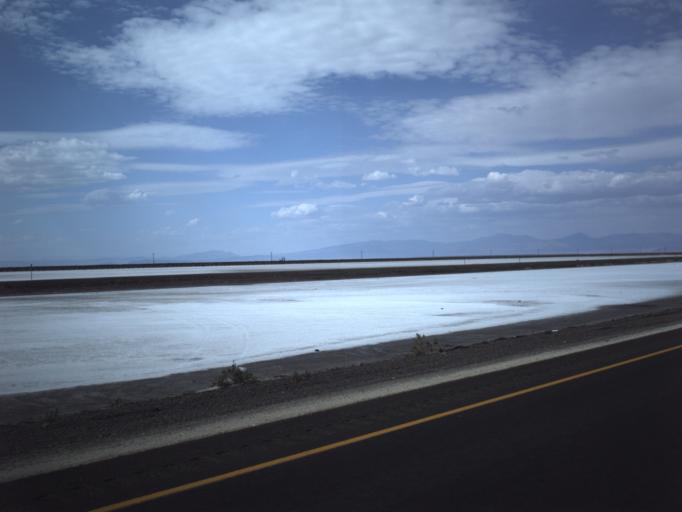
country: US
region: Utah
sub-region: Tooele County
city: Wendover
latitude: 40.7355
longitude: -113.6641
